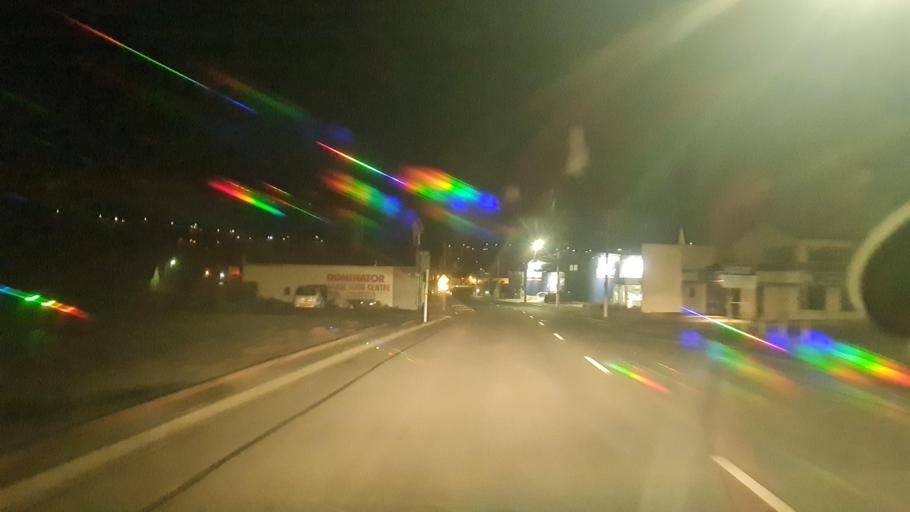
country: NZ
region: Otago
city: Oamaru
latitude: -45.0994
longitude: 170.9723
